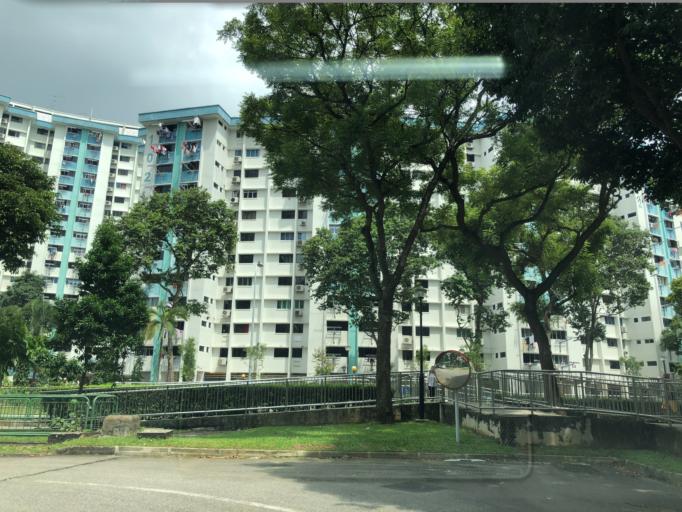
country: SG
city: Singapore
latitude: 1.3277
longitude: 103.8507
